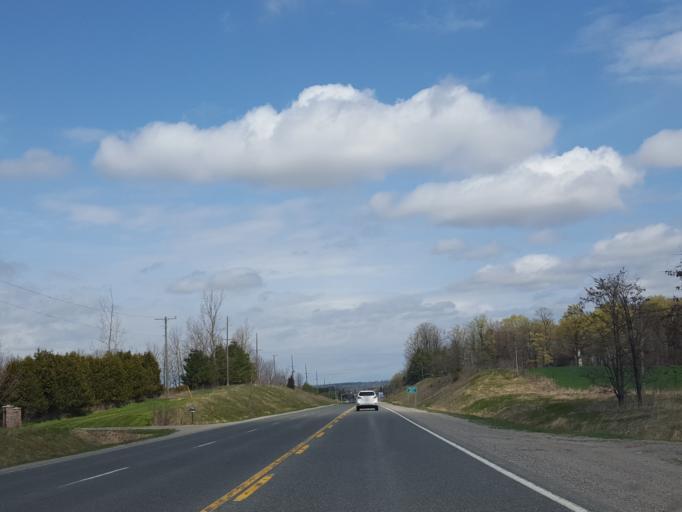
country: CA
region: Ontario
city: Newmarket
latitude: 44.1049
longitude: -79.3132
